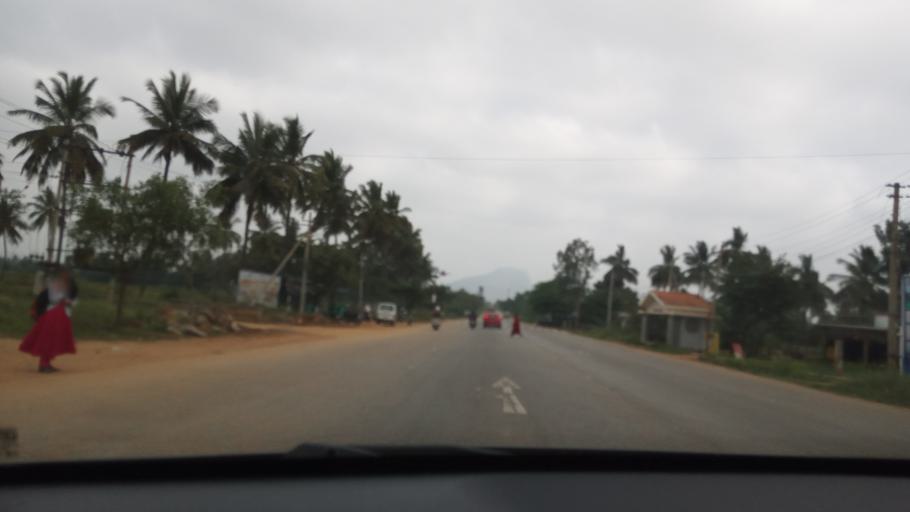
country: IN
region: Karnataka
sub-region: Chikkaballapur
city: Chintamani
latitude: 13.3047
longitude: 77.9733
